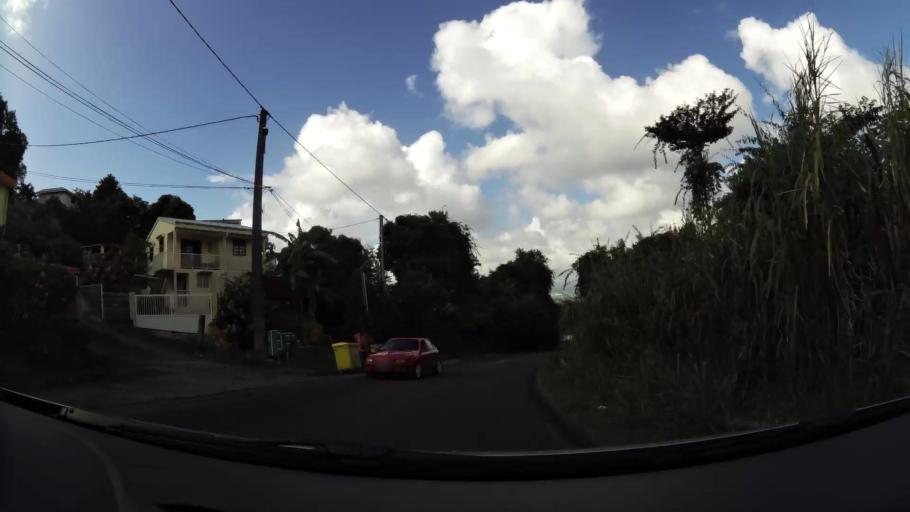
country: MQ
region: Martinique
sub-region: Martinique
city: Les Trois-Ilets
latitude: 14.5455
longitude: -61.0487
